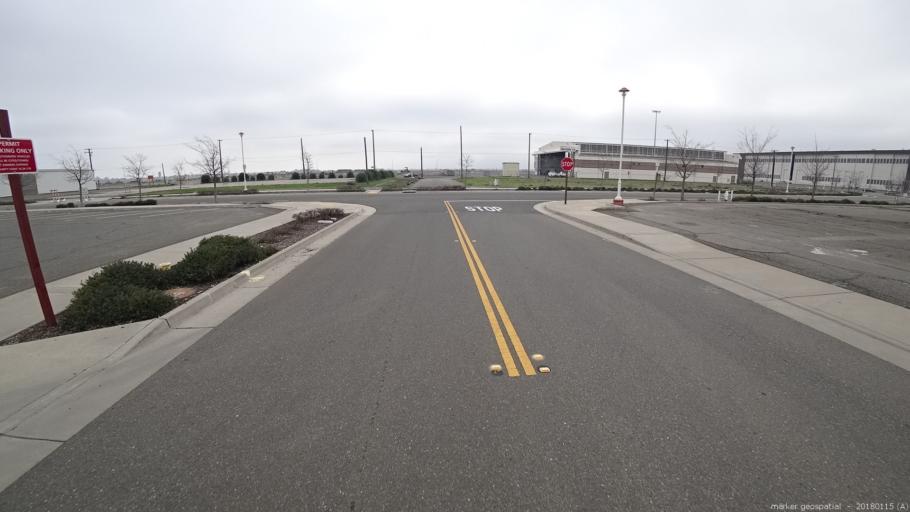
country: US
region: California
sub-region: Sacramento County
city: Rancho Cordova
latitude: 38.5653
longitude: -121.3014
